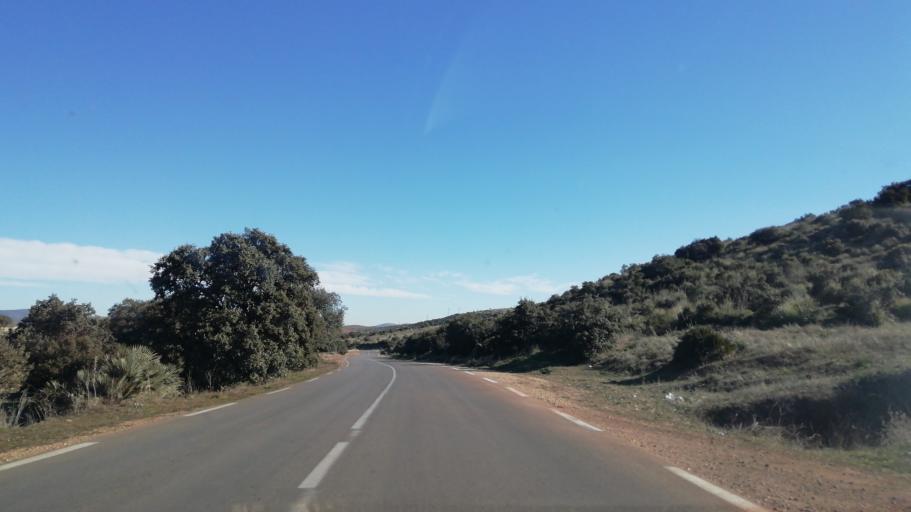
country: DZ
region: Tlemcen
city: Ouled Mimoun
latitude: 34.7565
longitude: -1.1503
